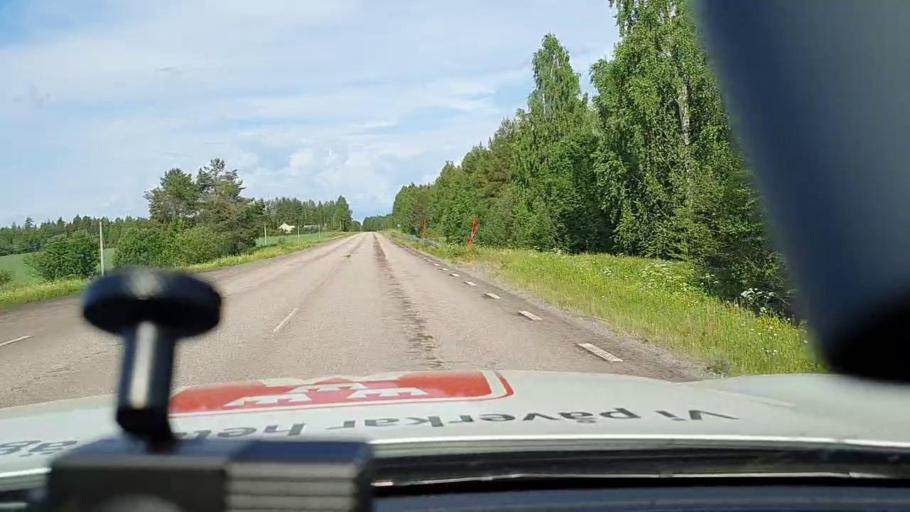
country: SE
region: Norrbotten
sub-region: Alvsbyns Kommun
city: AElvsbyn
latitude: 66.0184
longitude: 21.1477
